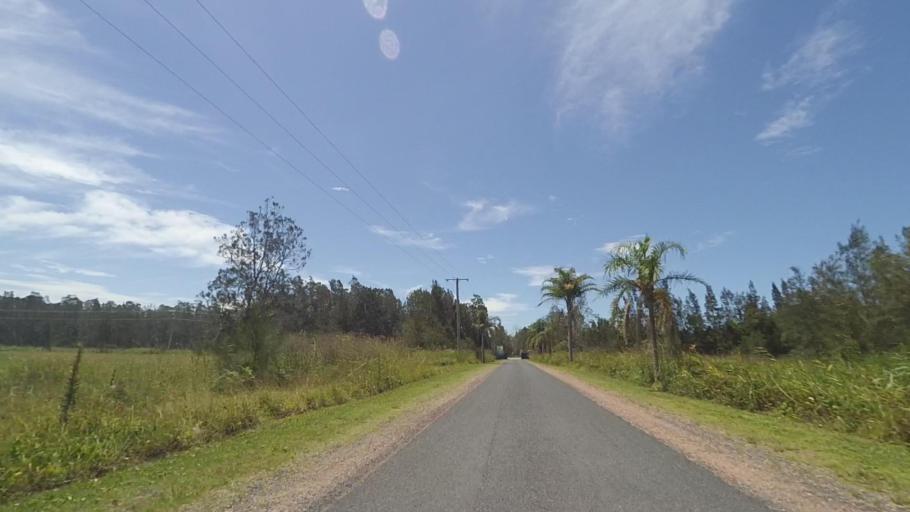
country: AU
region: New South Wales
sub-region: Port Stephens Shire
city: Anna Bay
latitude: -32.7688
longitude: 152.0024
